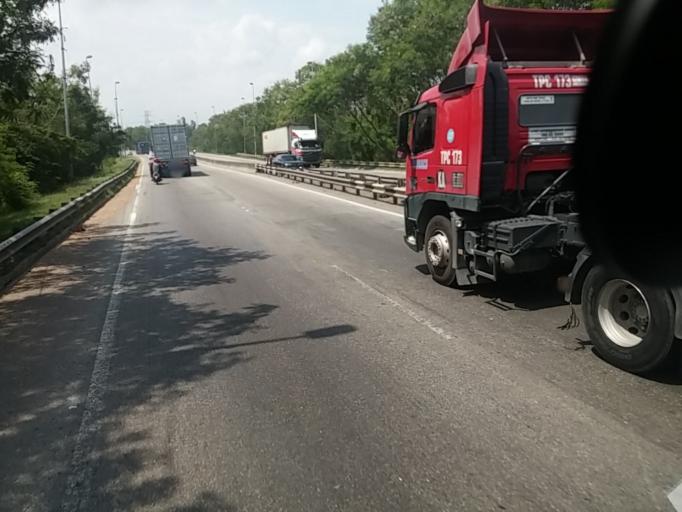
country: MY
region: Selangor
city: Klang
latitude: 2.9637
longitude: 101.3577
